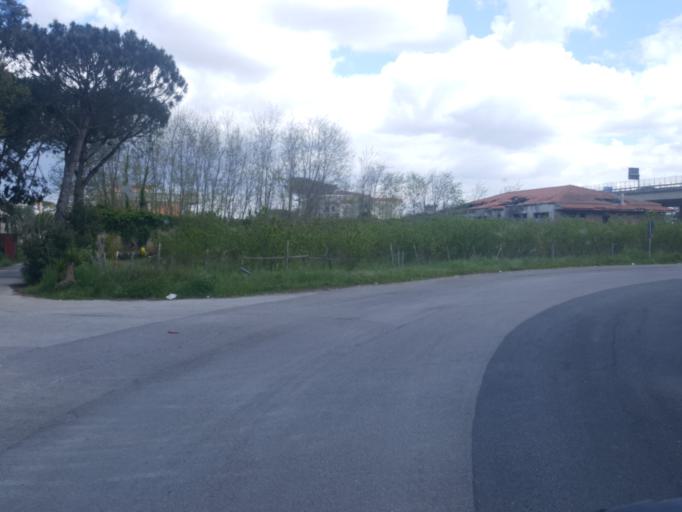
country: IT
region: Campania
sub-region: Provincia di Napoli
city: Torretta-Scalzapecora
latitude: 40.9323
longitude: 14.1076
